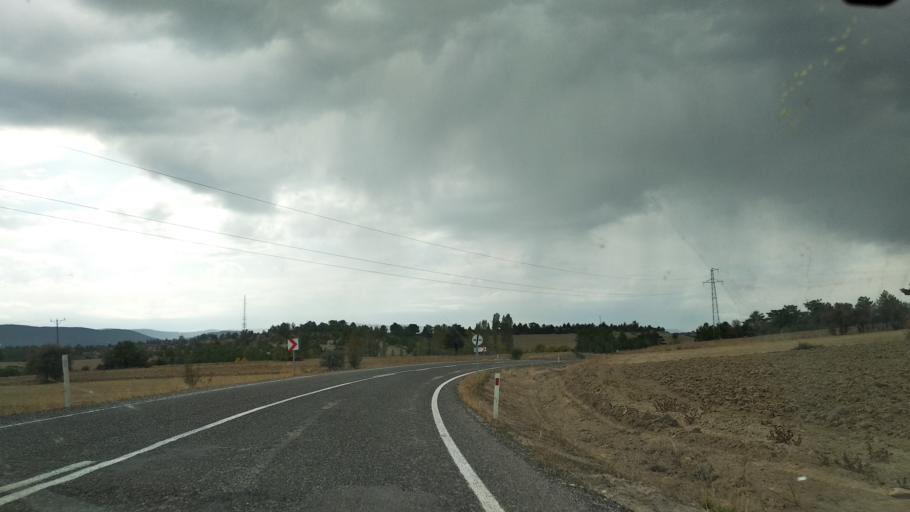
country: TR
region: Bolu
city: Seben
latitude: 40.3535
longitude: 31.4829
